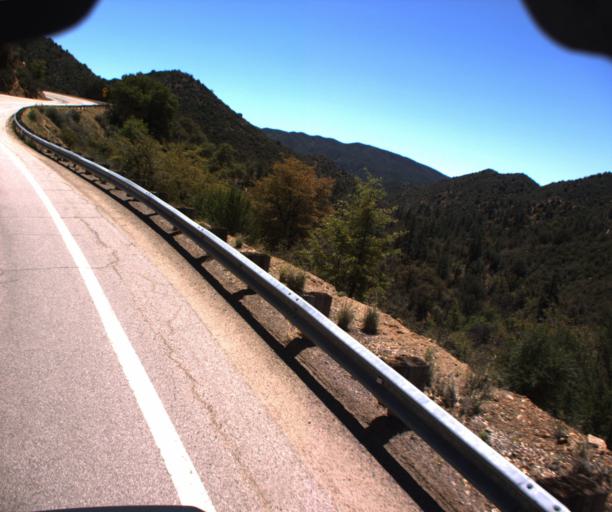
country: US
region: Arizona
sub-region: Yavapai County
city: Prescott
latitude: 34.4536
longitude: -112.5362
